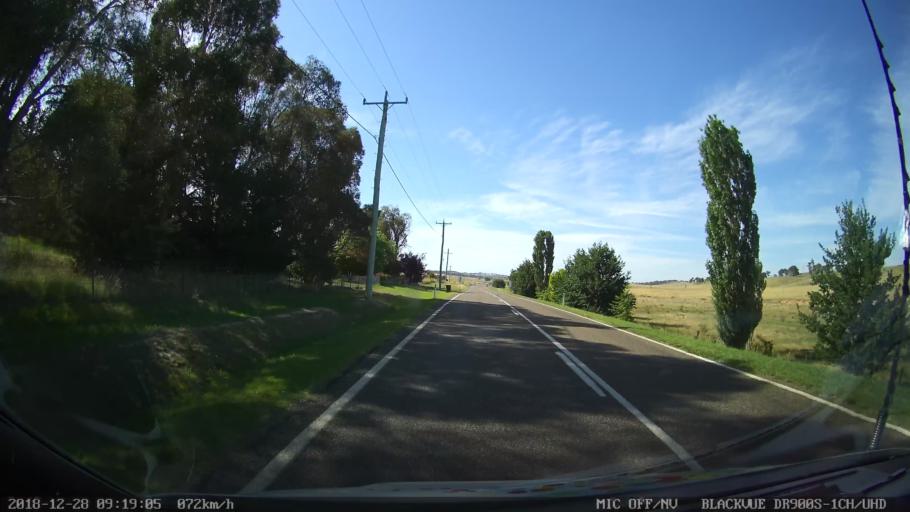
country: AU
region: New South Wales
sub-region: Upper Lachlan Shire
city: Crookwell
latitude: -34.3327
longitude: 149.3670
